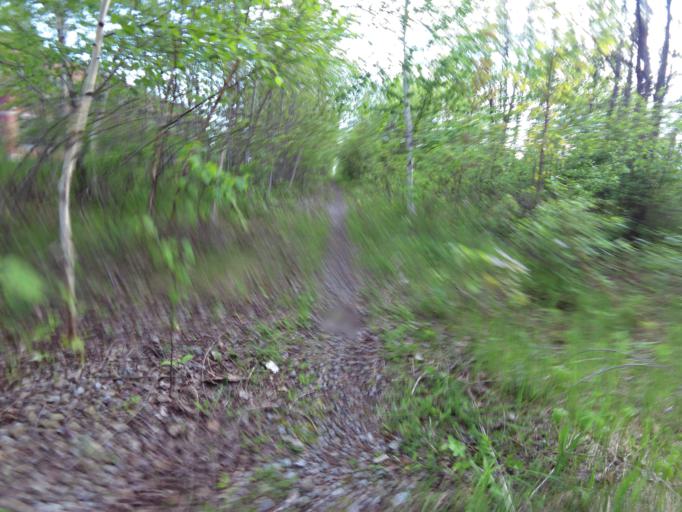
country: CA
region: Ontario
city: Bells Corners
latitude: 45.3242
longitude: -75.8385
